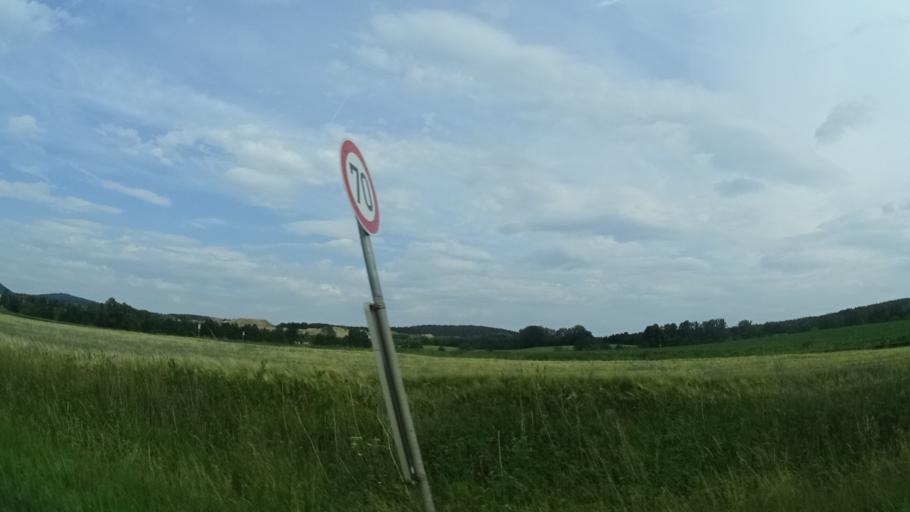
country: DE
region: Hesse
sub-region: Regierungsbezirk Kassel
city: Volkmarsen
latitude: 51.3973
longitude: 9.0916
